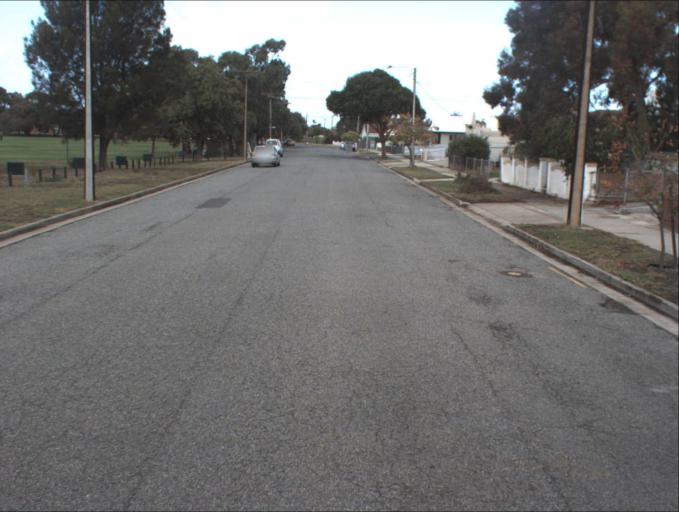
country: AU
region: South Australia
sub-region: Charles Sturt
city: West Lakes Shore
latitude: -34.8466
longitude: 138.4827
